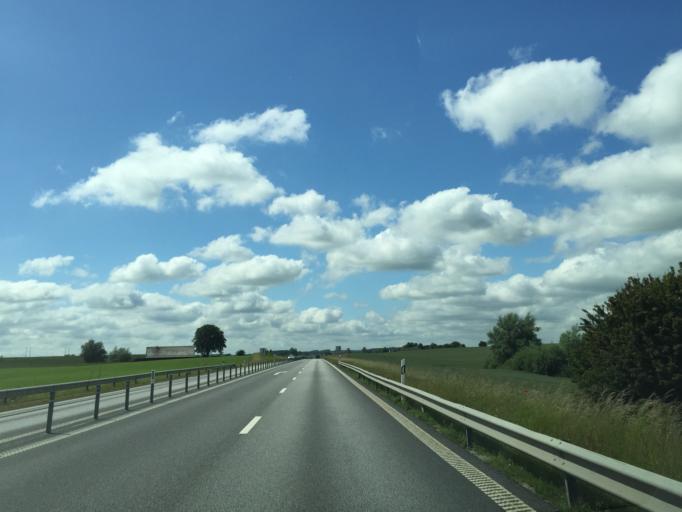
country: SE
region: Skane
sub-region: Skurups Kommun
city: Rydsgard
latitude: 55.4846
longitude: 13.5744
